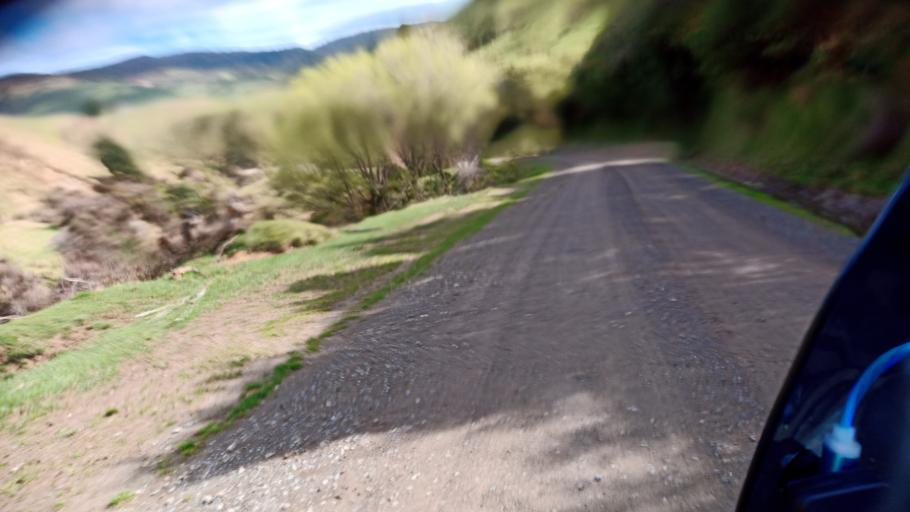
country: NZ
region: Hawke's Bay
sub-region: Wairoa District
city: Wairoa
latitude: -38.7358
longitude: 177.3038
